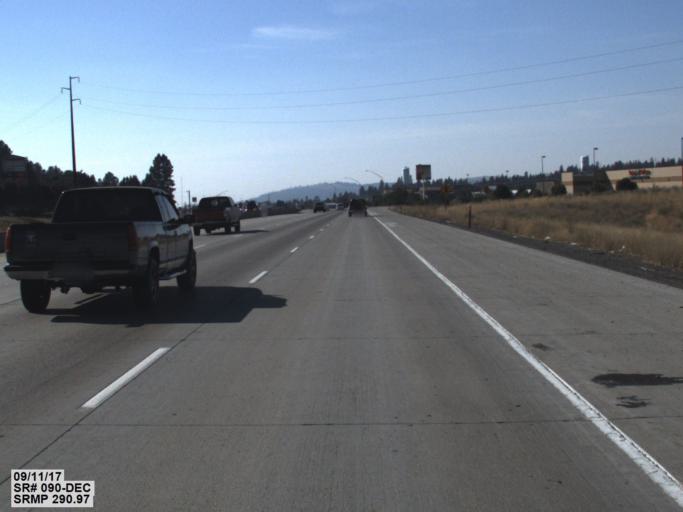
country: US
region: Washington
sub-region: Spokane County
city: Spokane Valley
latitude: 47.6732
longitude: -117.2159
